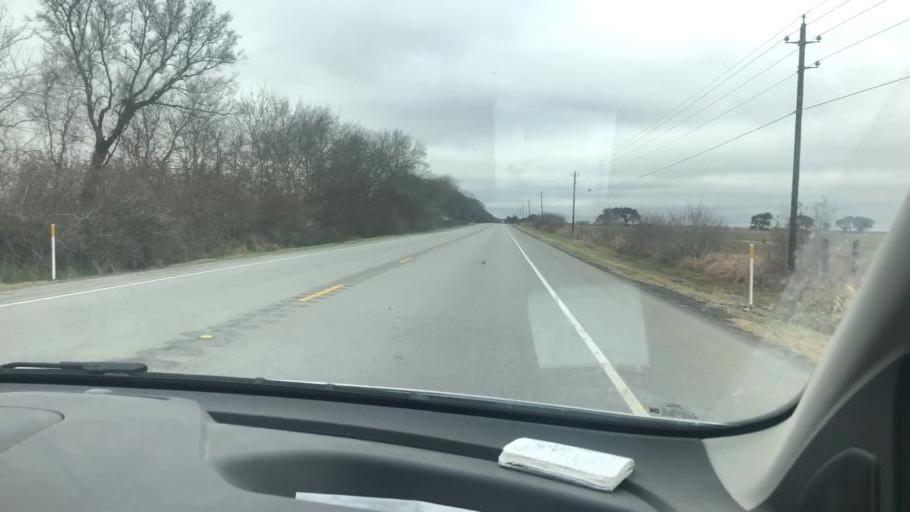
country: US
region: Texas
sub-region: Matagorda County
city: Bay City
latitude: 29.0783
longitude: -95.9730
